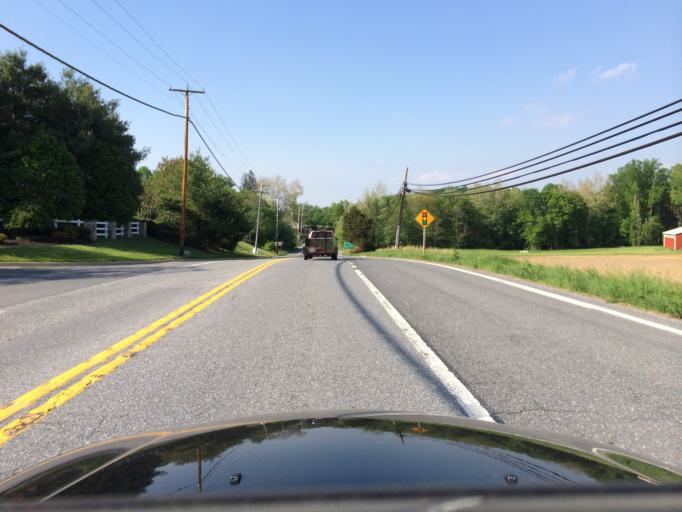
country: US
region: Maryland
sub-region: Carroll County
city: Sykesville
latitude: 39.3175
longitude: -77.0203
